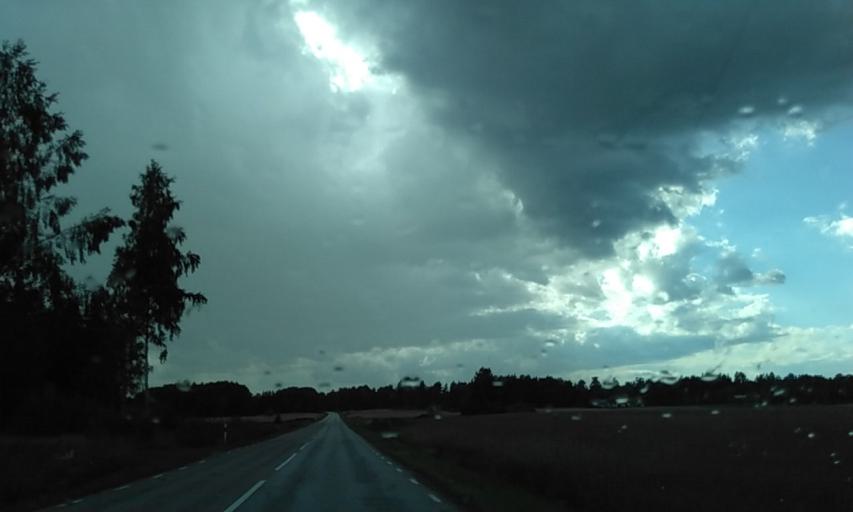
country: SE
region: Vaestra Goetaland
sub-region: Lidkopings Kommun
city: Lidkoping
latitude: 58.5030
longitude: 12.9789
